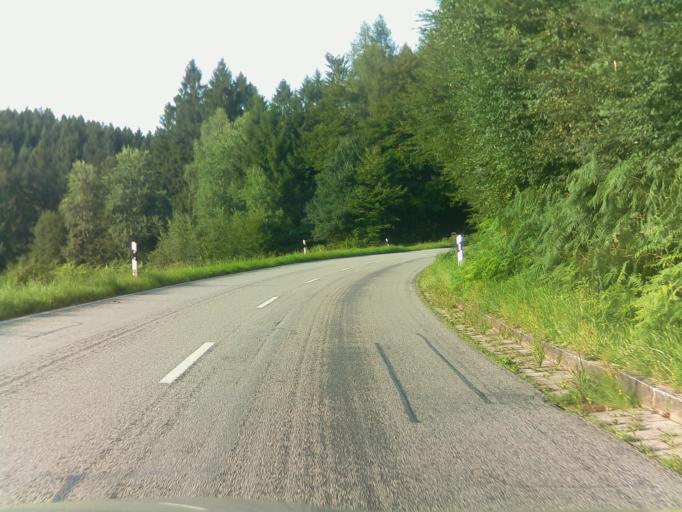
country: DE
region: Baden-Wuerttemberg
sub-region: Karlsruhe Region
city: Heddesbach
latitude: 49.4945
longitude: 8.8426
